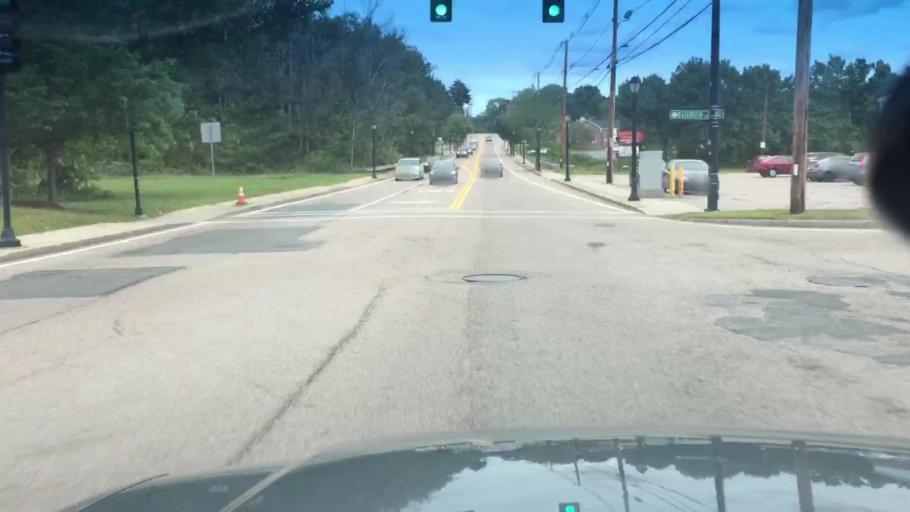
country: US
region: Massachusetts
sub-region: Norfolk County
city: Millis
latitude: 42.1608
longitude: -71.3732
